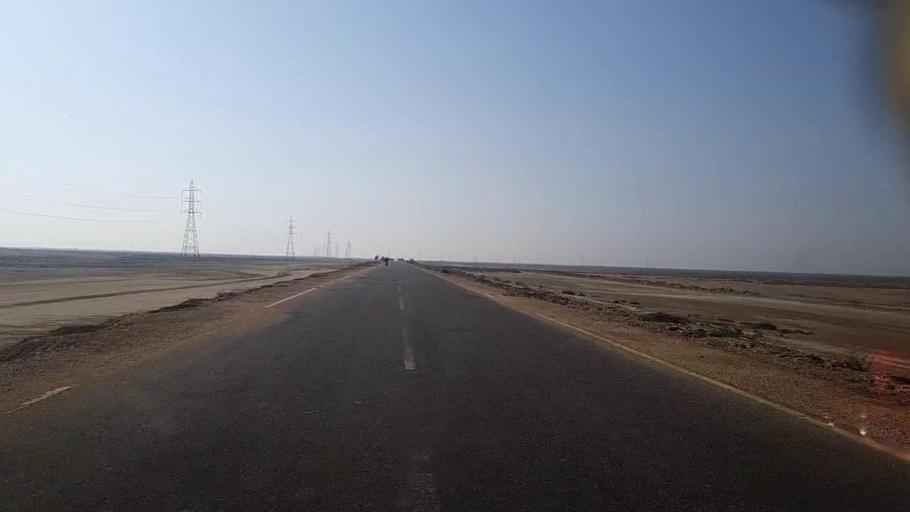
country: PK
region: Sindh
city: Mirpur Sakro
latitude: 24.6087
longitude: 67.4971
